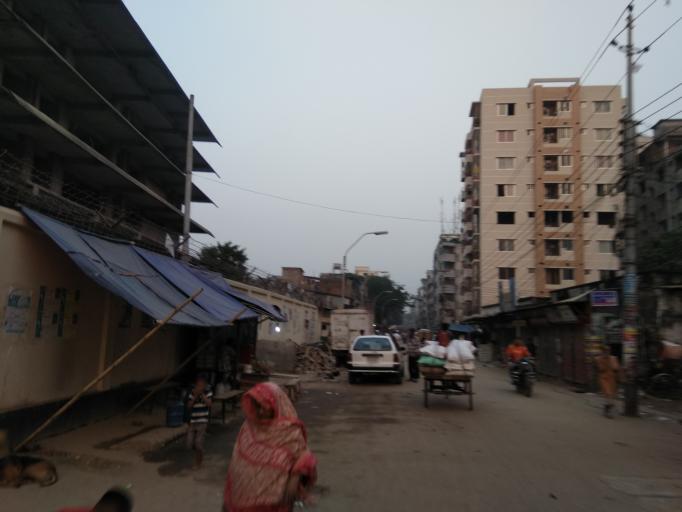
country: BD
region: Dhaka
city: Tungi
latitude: 23.8136
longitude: 90.3704
